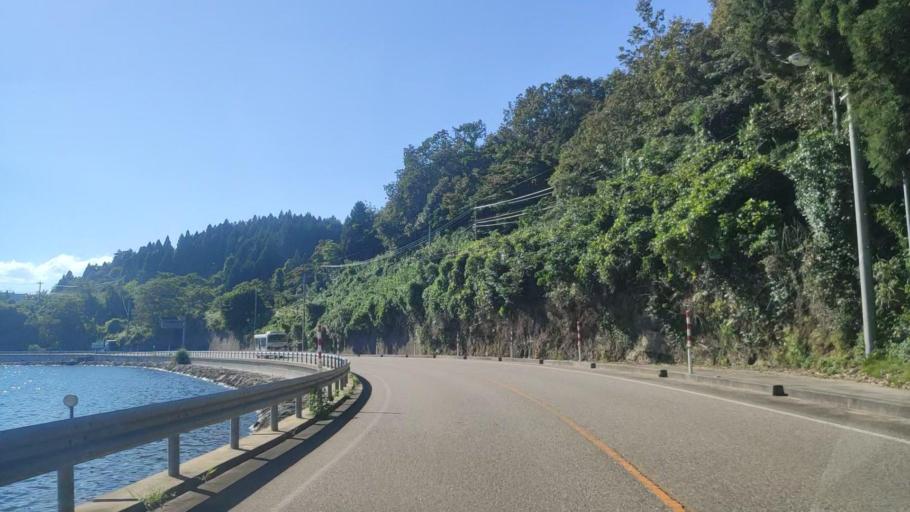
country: JP
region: Ishikawa
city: Nanao
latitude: 37.2354
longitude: 136.9560
